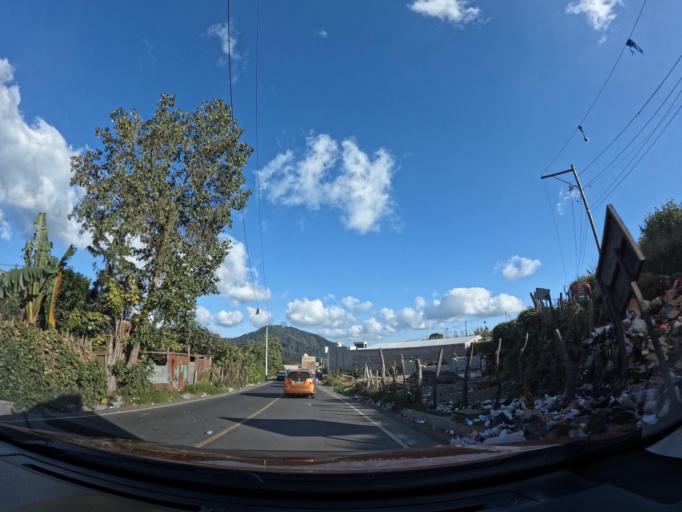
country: GT
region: Sacatepequez
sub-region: Municipio de Santa Maria de Jesus
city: Santa Maria de Jesus
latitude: 14.4883
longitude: -90.7082
